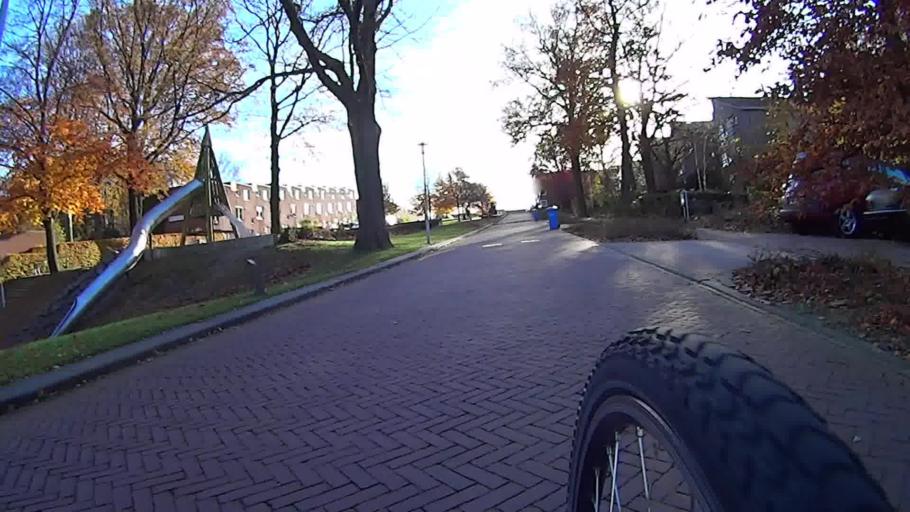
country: NL
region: Utrecht
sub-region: Gemeente Amersfoort
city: Amersfoort
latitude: 52.1451
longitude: 5.3592
